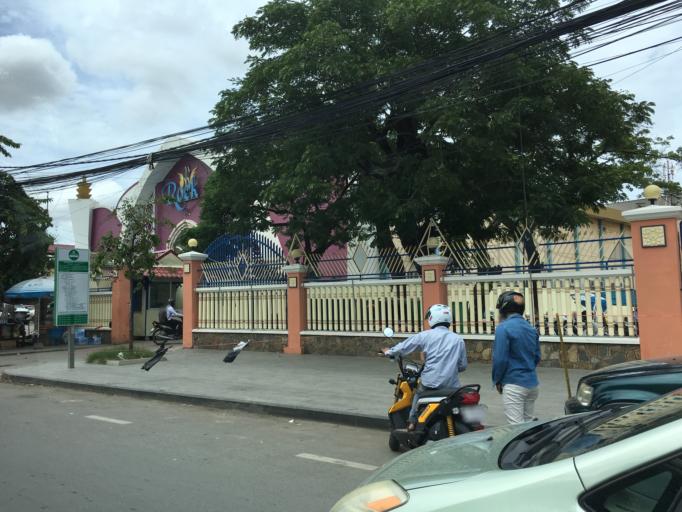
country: KH
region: Phnom Penh
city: Phnom Penh
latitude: 11.5360
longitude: 104.9236
